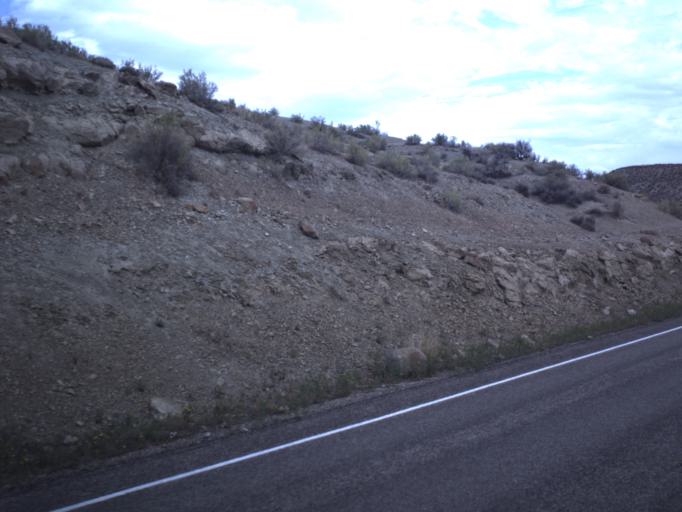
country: US
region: Colorado
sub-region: Rio Blanco County
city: Rangely
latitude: 40.0623
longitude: -109.1975
